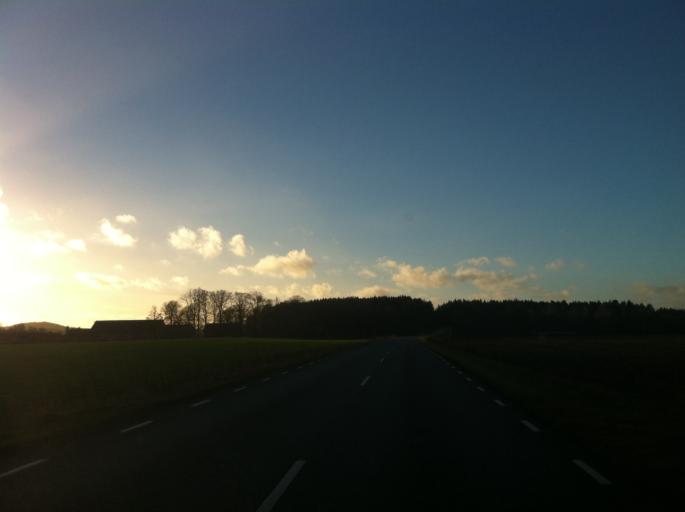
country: SE
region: Skane
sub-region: Ostra Goinge Kommun
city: Knislinge
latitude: 56.1880
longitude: 14.0474
